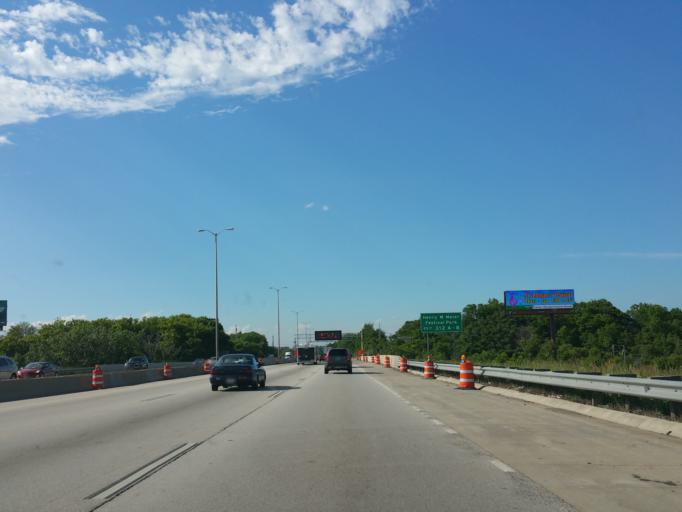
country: US
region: Wisconsin
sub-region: Milwaukee County
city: Milwaukee
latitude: 42.9940
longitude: -87.9149
